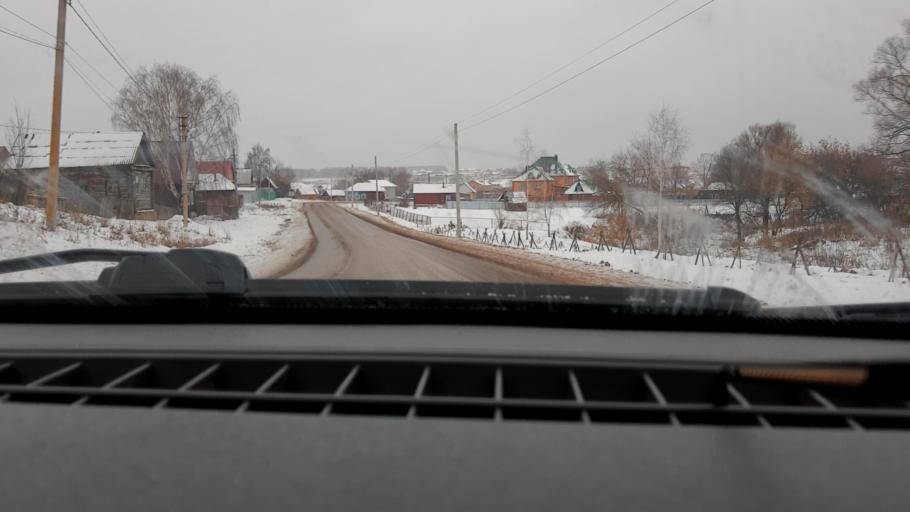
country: RU
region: Bashkortostan
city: Kabakovo
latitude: 54.7035
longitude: 56.2494
